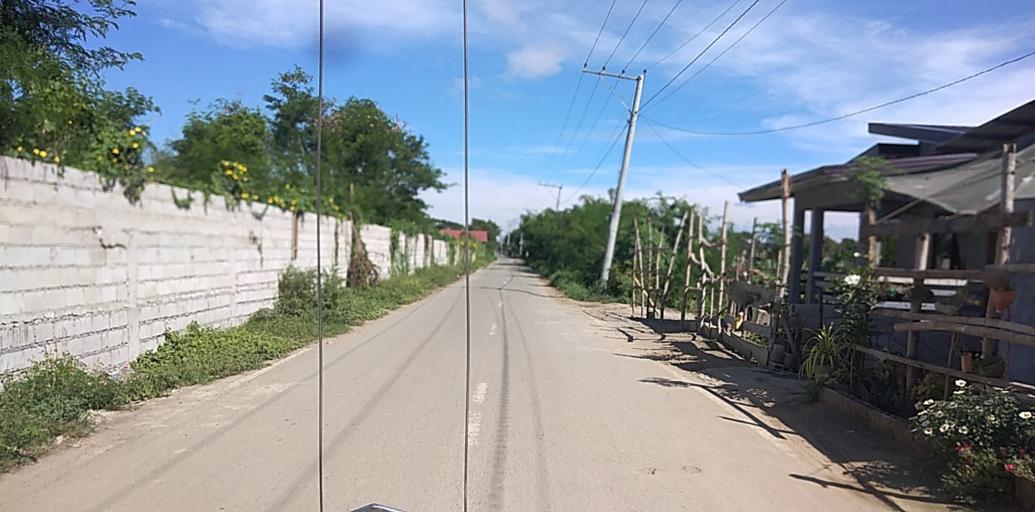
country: PH
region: Central Luzon
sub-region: Province of Pampanga
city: Candaba
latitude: 15.0767
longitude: 120.8078
